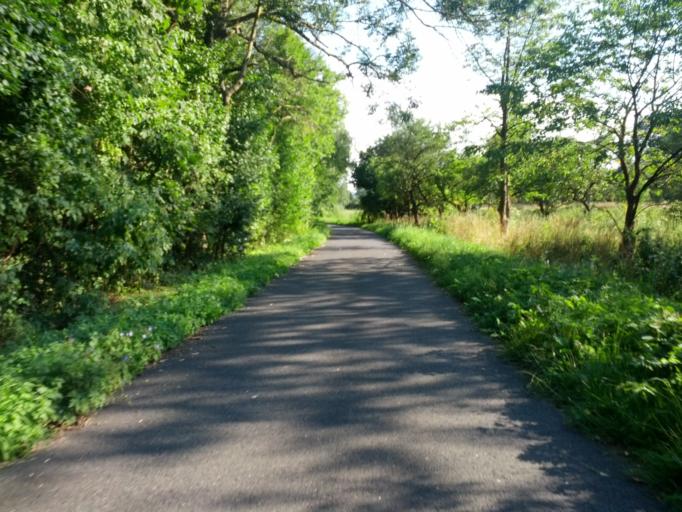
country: DE
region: Thuringia
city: Creuzburg
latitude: 51.0563
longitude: 10.2526
